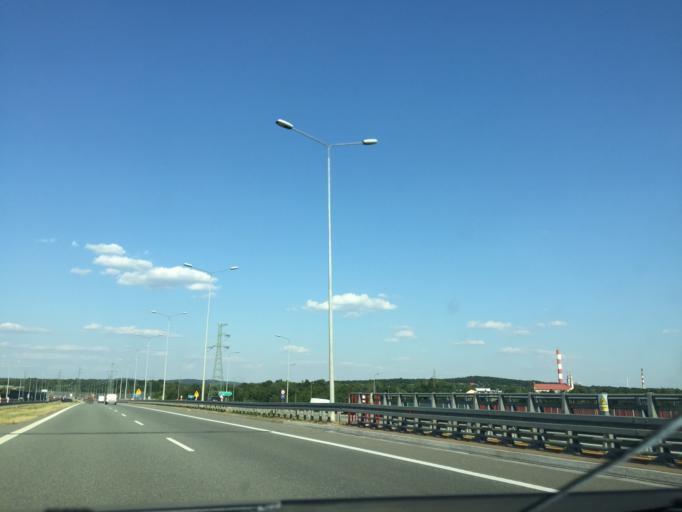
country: PL
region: Swietokrzyskie
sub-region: Powiat kielecki
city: Kostomloty Pierwsze
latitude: 50.9084
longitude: 20.5798
